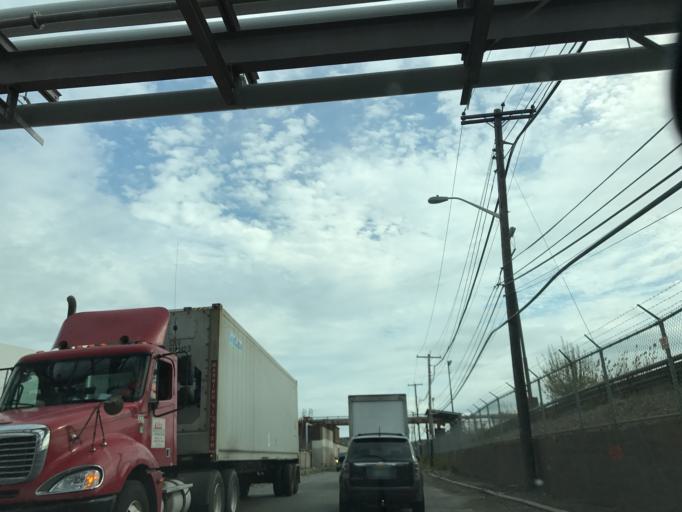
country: US
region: Massachusetts
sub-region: Middlesex County
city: Everett
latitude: 42.3960
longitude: -71.0596
